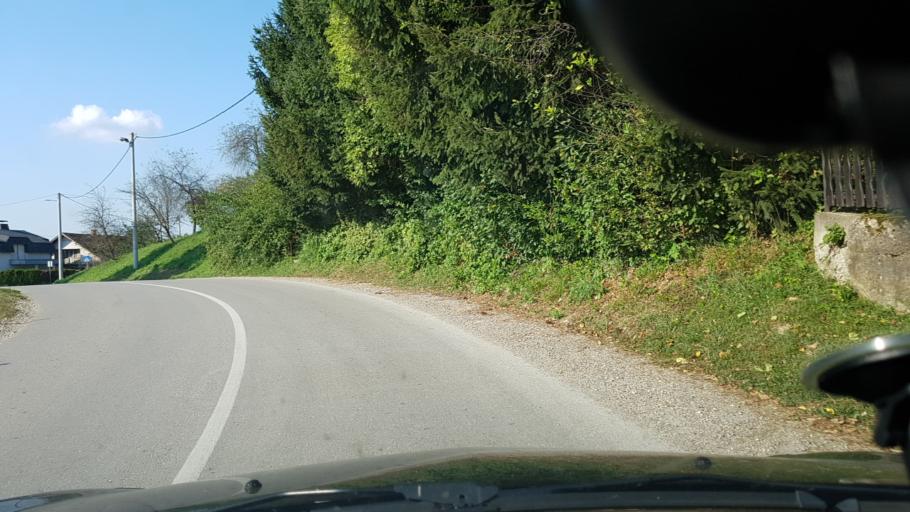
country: HR
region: Zagrebacka
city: Pojatno
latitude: 45.9434
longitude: 15.7294
